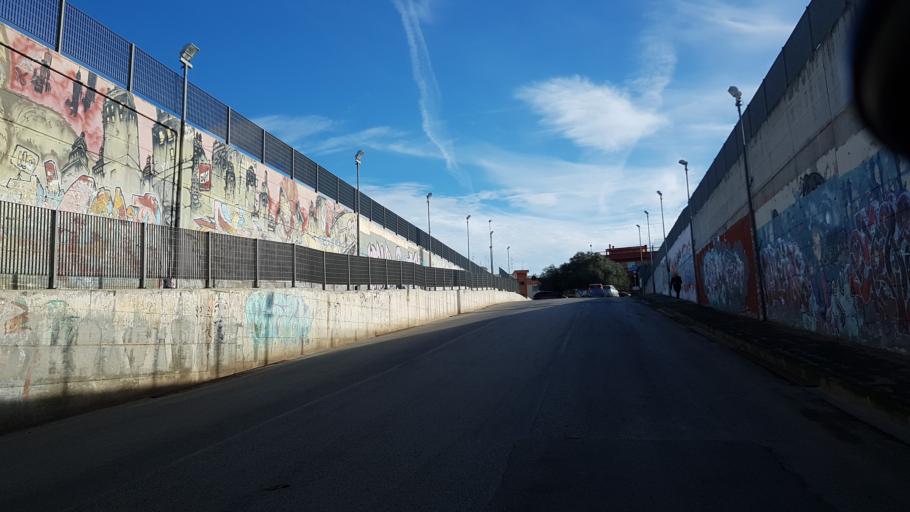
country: IT
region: Apulia
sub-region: Provincia di Bari
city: Gioia del Colle
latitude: 40.8006
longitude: 16.9167
